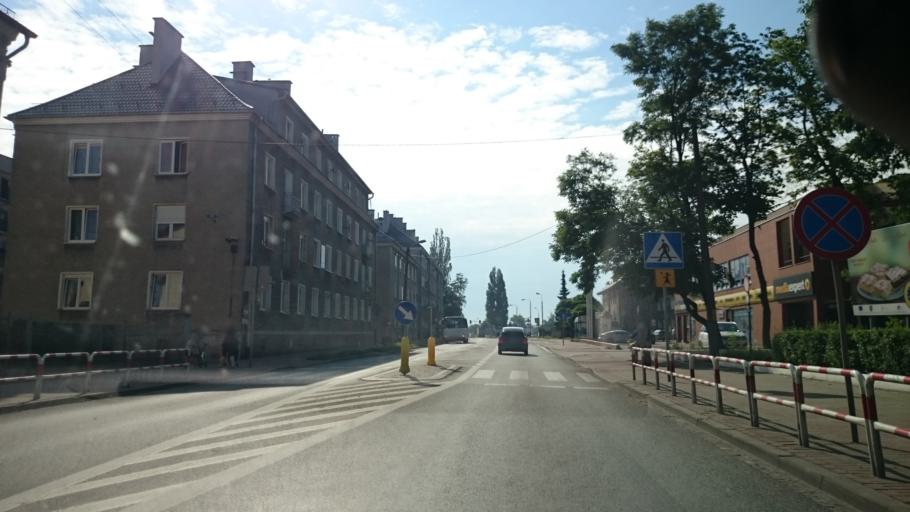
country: PL
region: Opole Voivodeship
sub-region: Powiat strzelecki
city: Strzelce Opolskie
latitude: 50.5081
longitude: 18.3085
